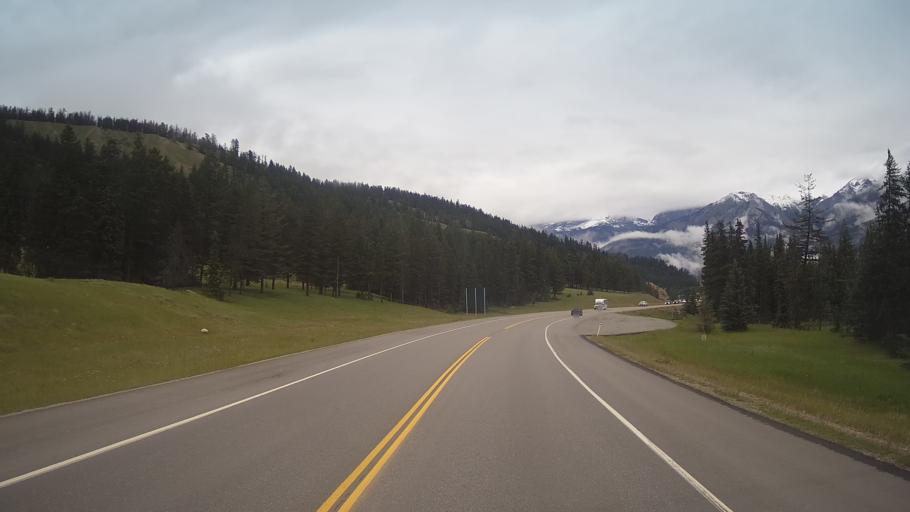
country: CA
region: Alberta
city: Jasper Park Lodge
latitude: 52.9034
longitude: -118.0657
